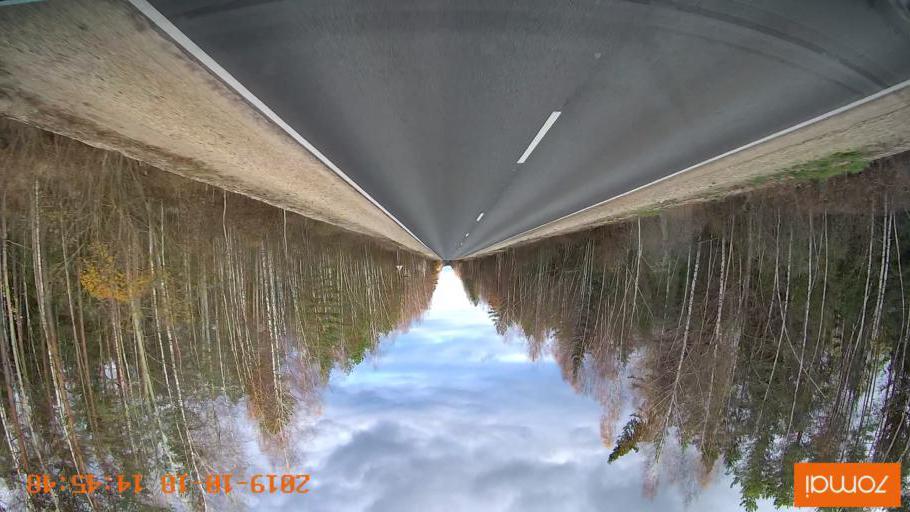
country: RU
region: Vladimir
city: Velikodvorskiy
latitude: 55.3608
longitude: 40.6796
